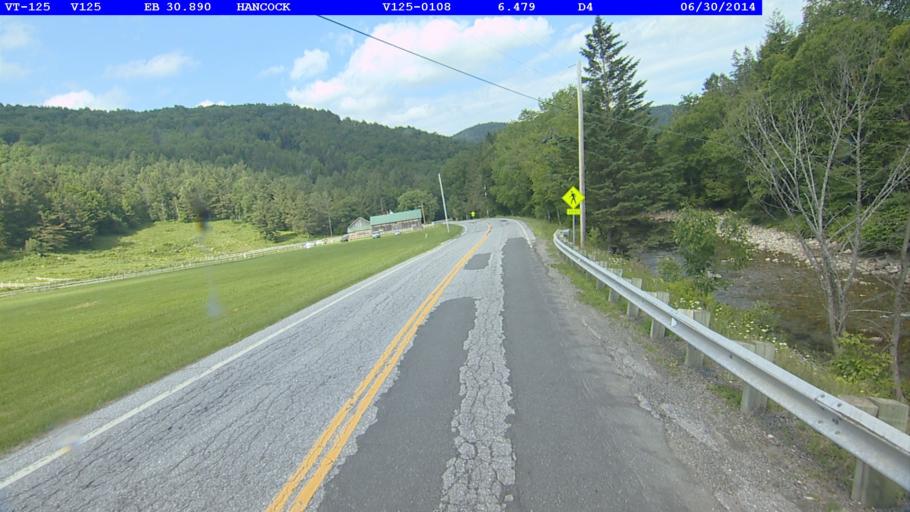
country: US
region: Vermont
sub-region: Orange County
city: Randolph
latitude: 43.9262
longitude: -72.8552
